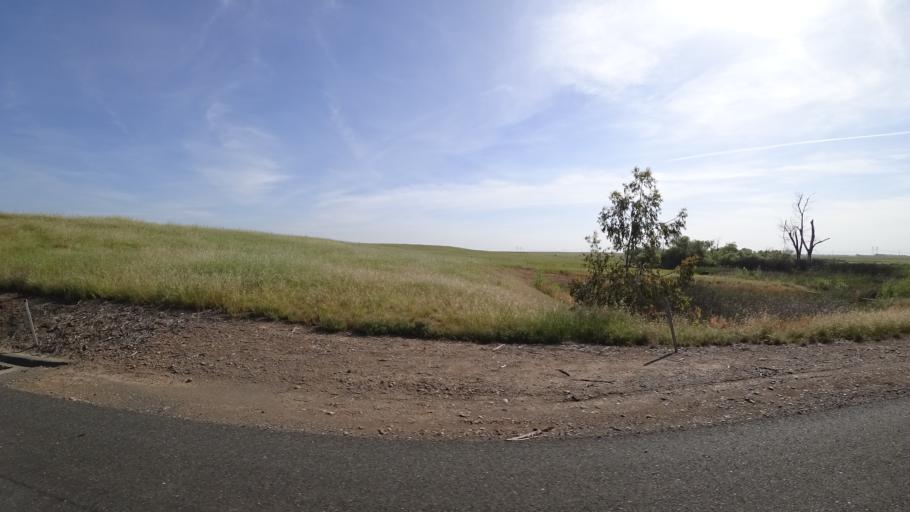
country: US
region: California
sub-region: Butte County
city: Thermalito
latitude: 39.5912
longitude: -121.6407
